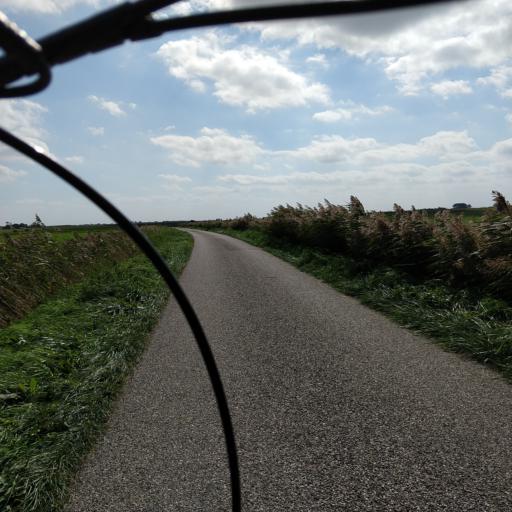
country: NL
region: Zeeland
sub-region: Gemeente Noord-Beveland
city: Kamperland
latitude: 51.5937
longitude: 3.7619
